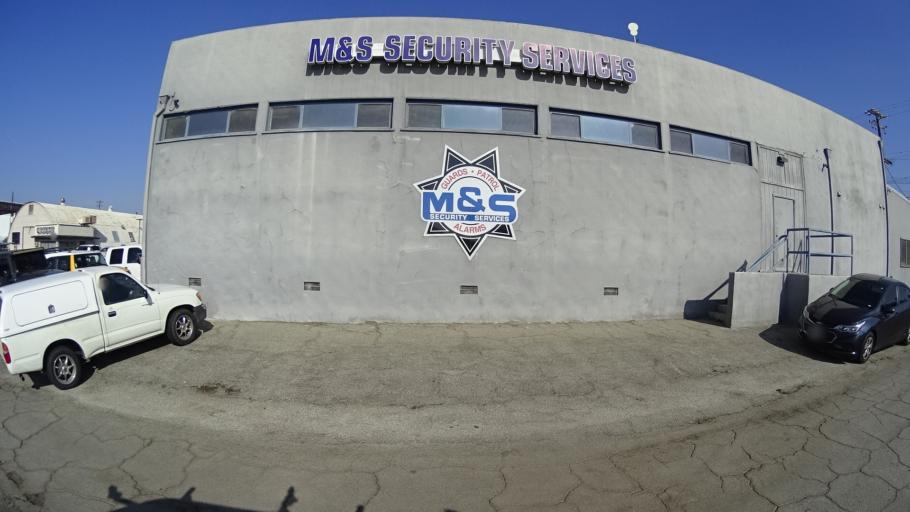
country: US
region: California
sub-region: Kern County
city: Bakersfield
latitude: 35.3858
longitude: -119.0161
